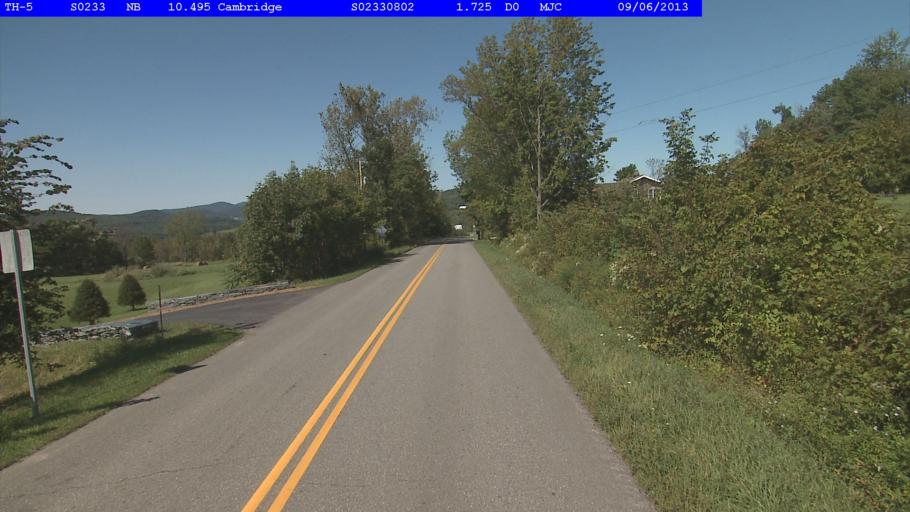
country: US
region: Vermont
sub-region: Chittenden County
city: Jericho
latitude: 44.6066
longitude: -72.8565
